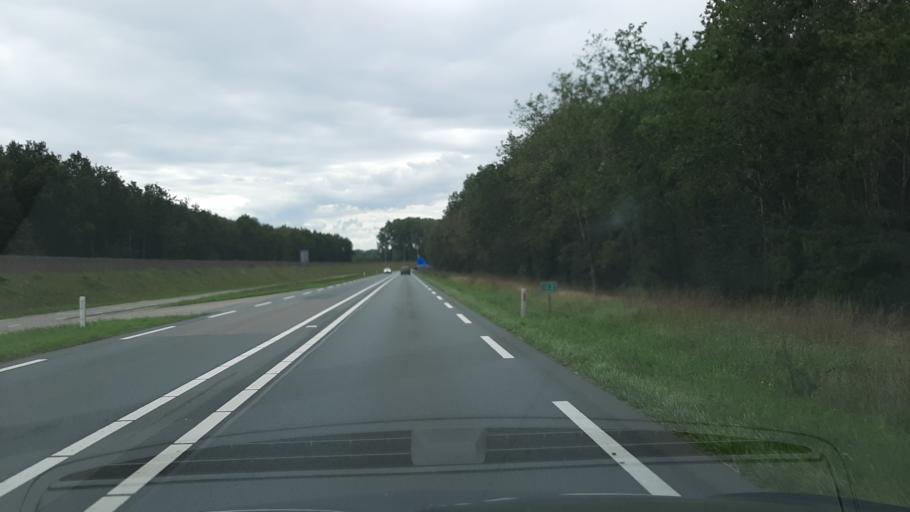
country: NL
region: Overijssel
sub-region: Gemeente Kampen
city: Kampen
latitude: 52.5400
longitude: 5.9290
